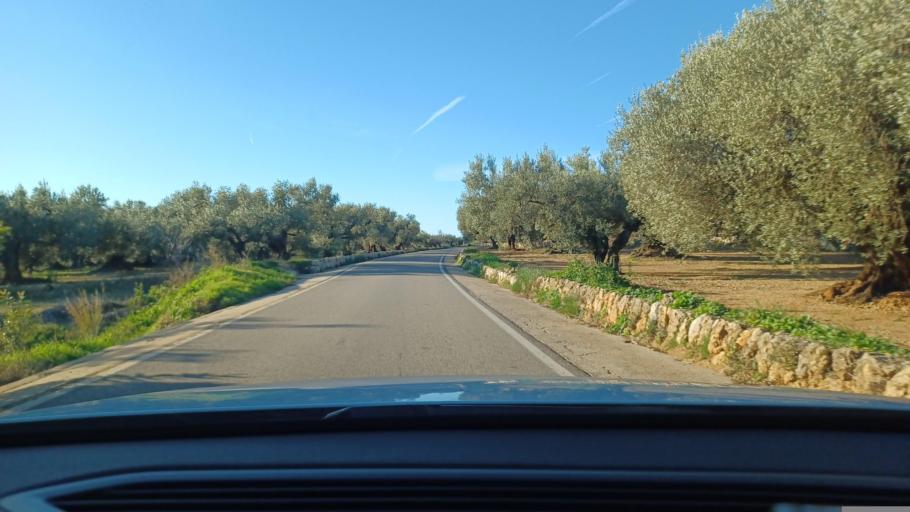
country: ES
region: Catalonia
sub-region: Provincia de Tarragona
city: Mas de Barberans
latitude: 40.7202
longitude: 0.3644
